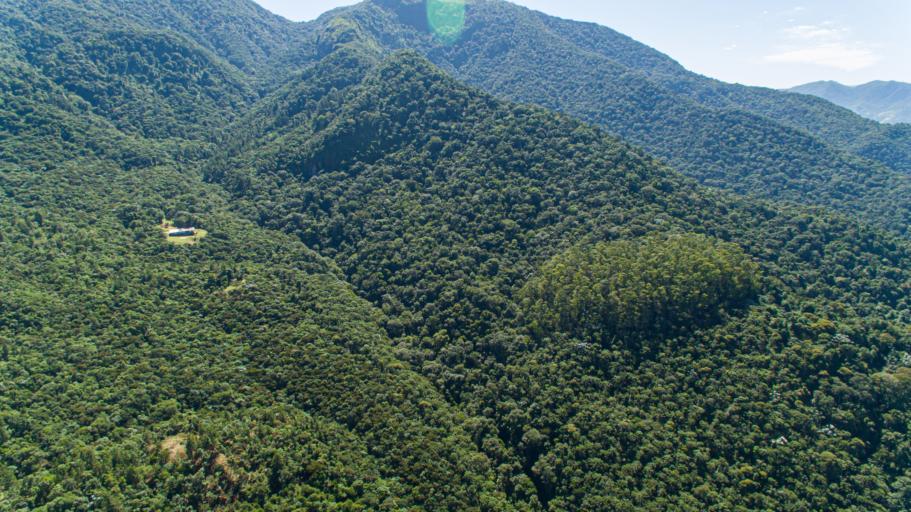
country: BR
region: Minas Gerais
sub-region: Camanducaia
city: Camanducaia
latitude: -22.8921
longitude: -45.9720
